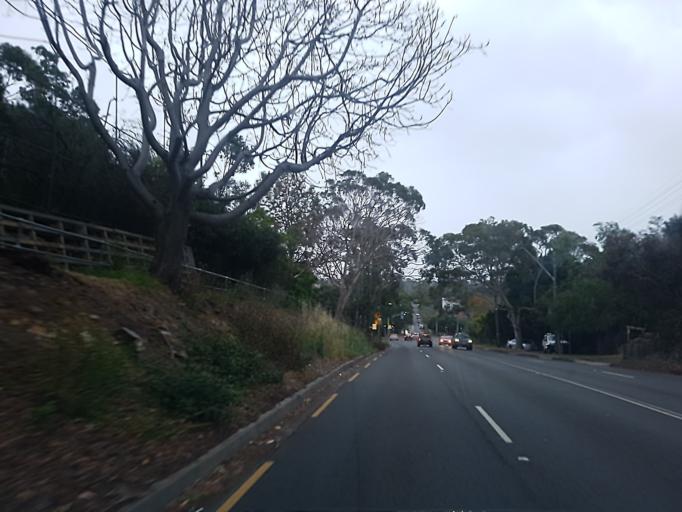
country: AU
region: New South Wales
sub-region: Willoughby
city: Castle Cove
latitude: -33.7932
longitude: 151.2076
